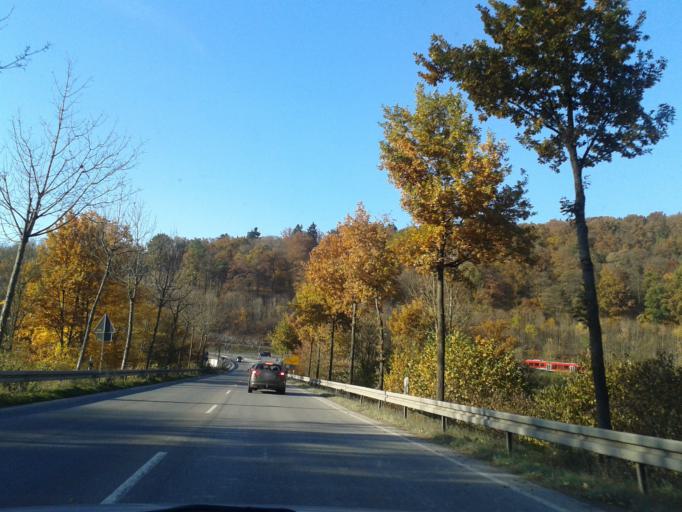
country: DE
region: North Rhine-Westphalia
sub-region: Regierungsbezirk Arnsberg
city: Olsberg
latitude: 51.3637
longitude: 8.4528
